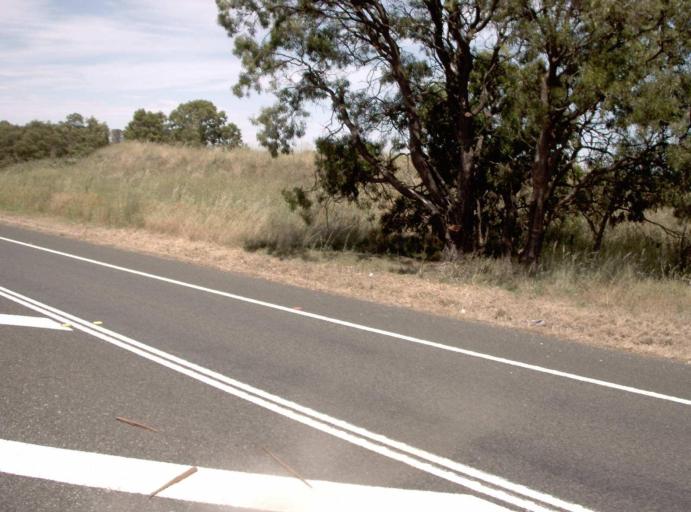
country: AU
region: Victoria
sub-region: Wellington
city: Heyfield
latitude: -38.1142
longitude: 146.8763
